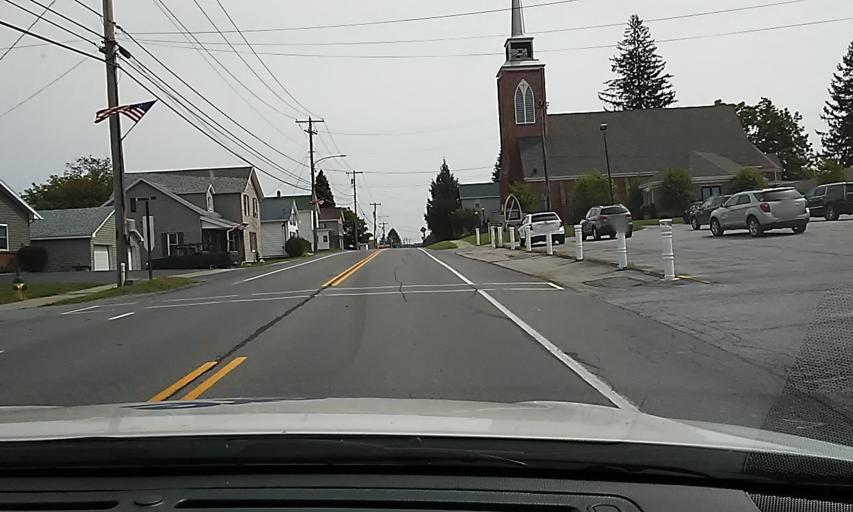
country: US
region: Pennsylvania
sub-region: Elk County
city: Saint Marys
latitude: 41.3620
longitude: -78.6022
